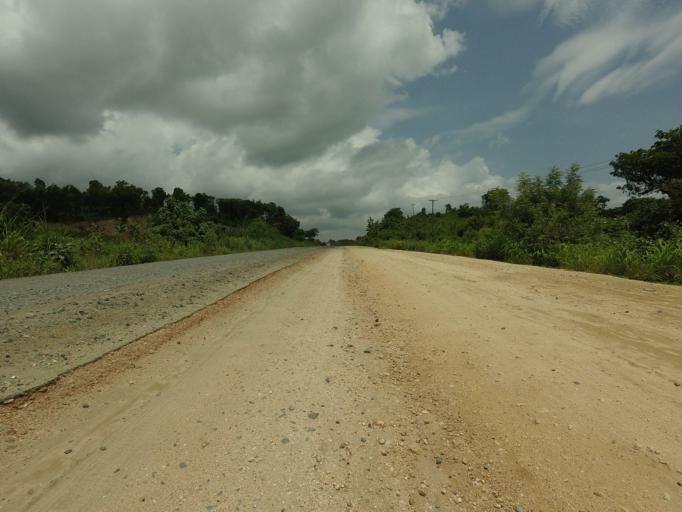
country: GH
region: Volta
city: Ho
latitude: 6.6738
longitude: 0.3122
